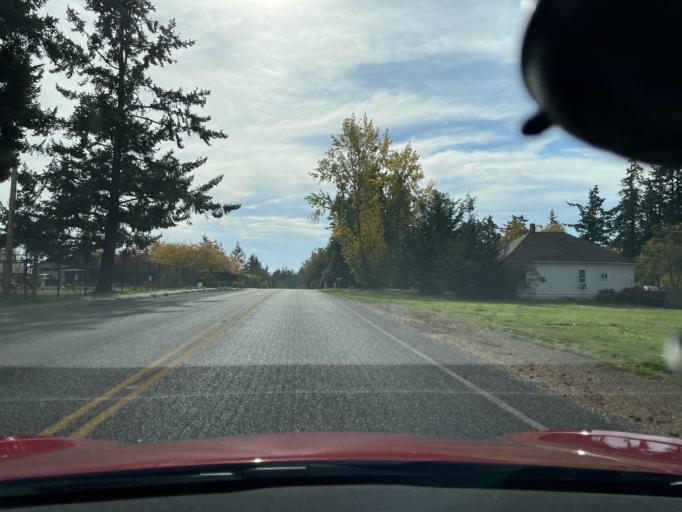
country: US
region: Washington
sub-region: San Juan County
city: Friday Harbor
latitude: 48.5260
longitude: -123.0177
